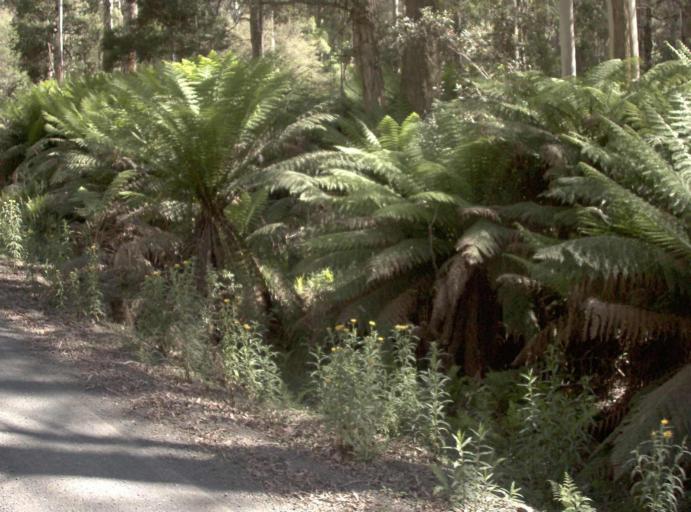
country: AU
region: New South Wales
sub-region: Bombala
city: Bombala
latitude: -37.2156
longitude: 148.7463
